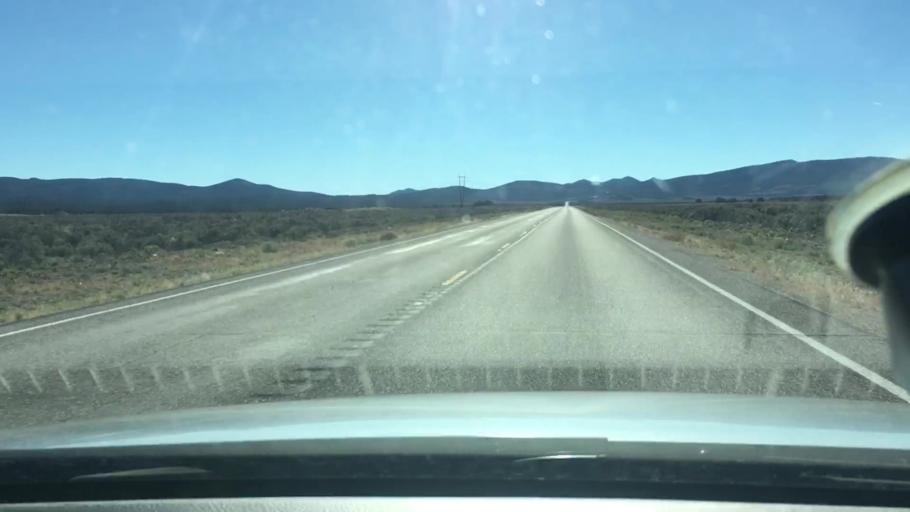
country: US
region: Nevada
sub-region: White Pine County
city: Ely
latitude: 38.8759
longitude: -115.2145
